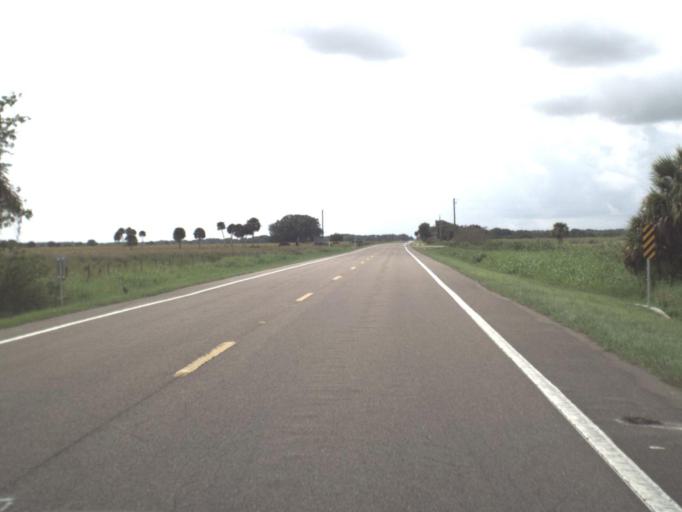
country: US
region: Florida
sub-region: Sarasota County
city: North Port
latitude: 27.1933
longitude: -82.1201
